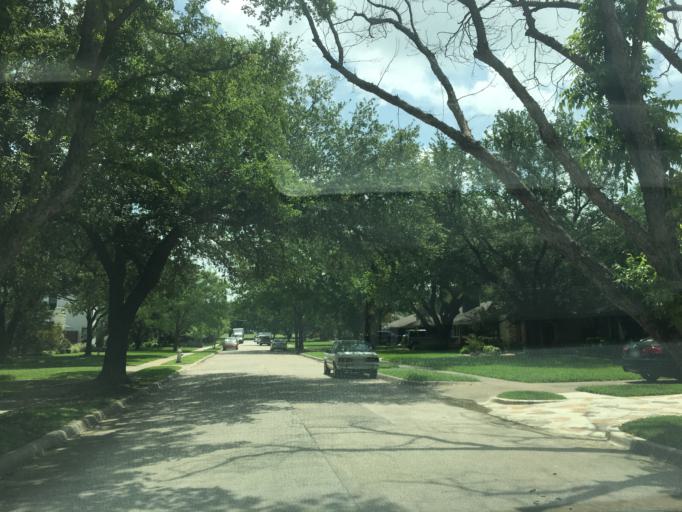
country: US
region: Texas
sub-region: Dallas County
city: University Park
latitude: 32.8725
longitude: -96.7937
